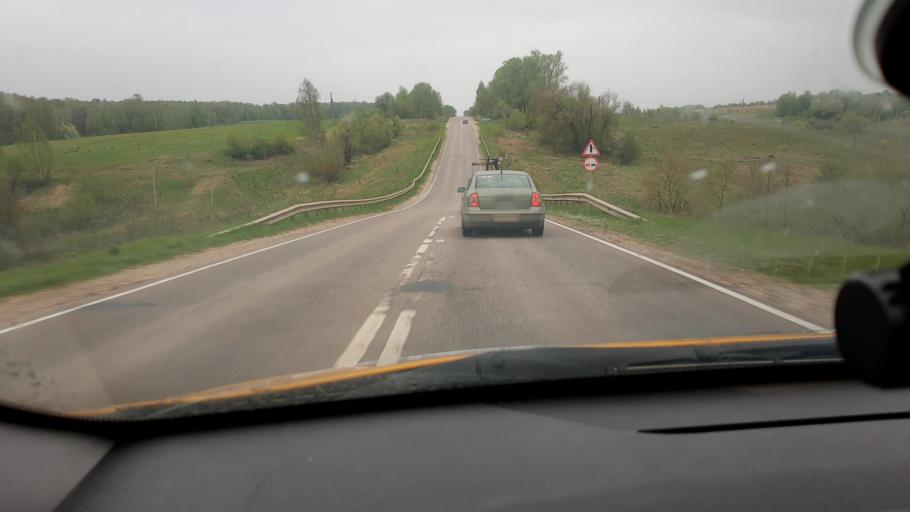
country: RU
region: Tula
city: Zaokskiy
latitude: 54.7800
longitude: 37.4346
